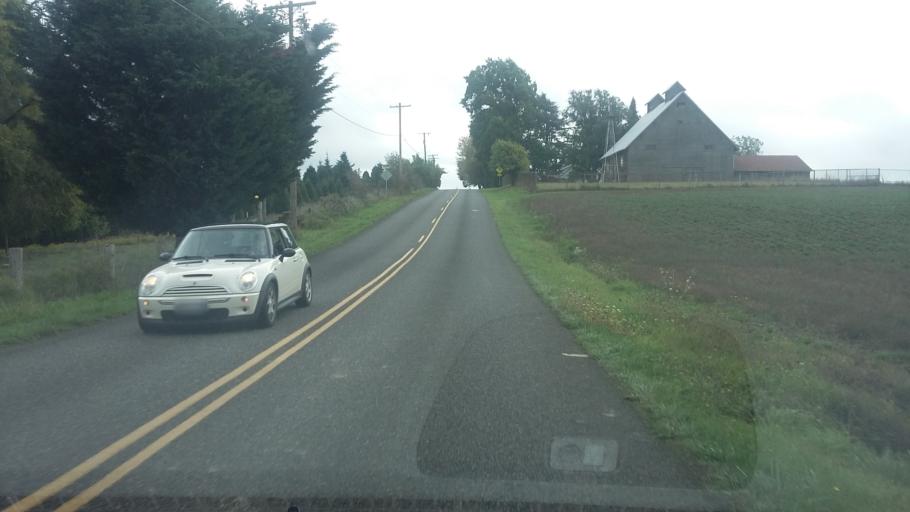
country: US
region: Washington
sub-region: Clark County
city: La Center
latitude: 45.8296
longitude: -122.6827
